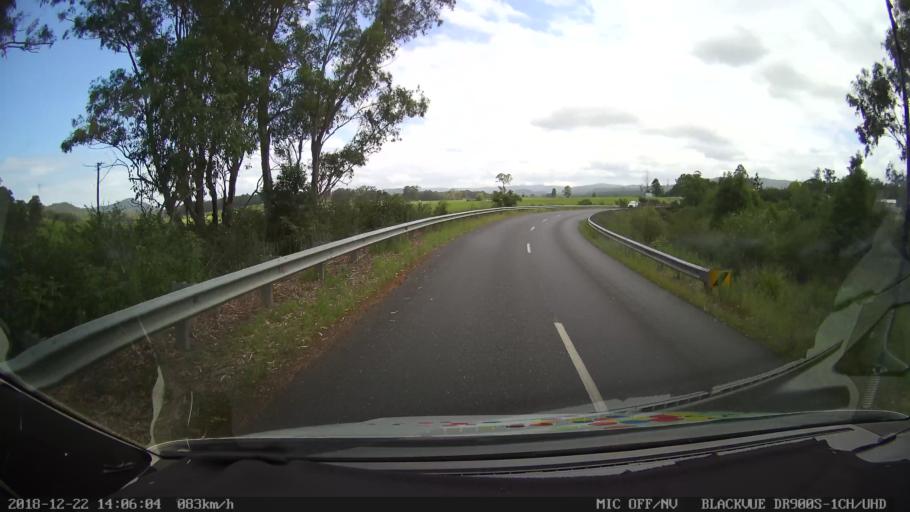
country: AU
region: New South Wales
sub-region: Clarence Valley
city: Coutts Crossing
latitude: -29.9519
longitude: 152.7288
